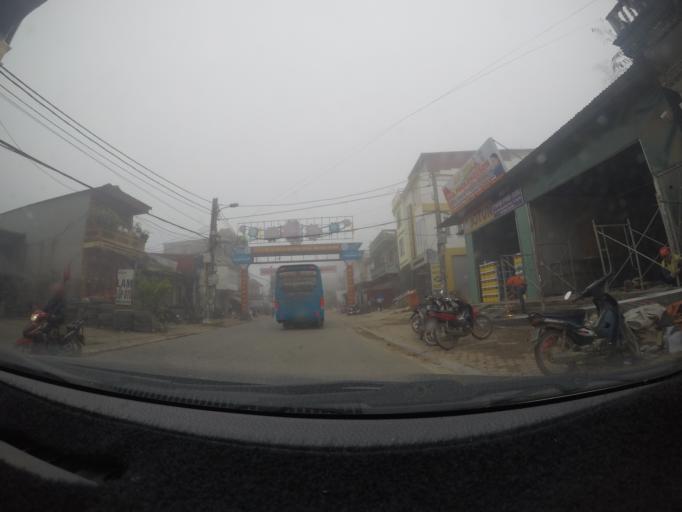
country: VN
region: Lao Cai
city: Sa Pa
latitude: 22.3407
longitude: 103.8549
